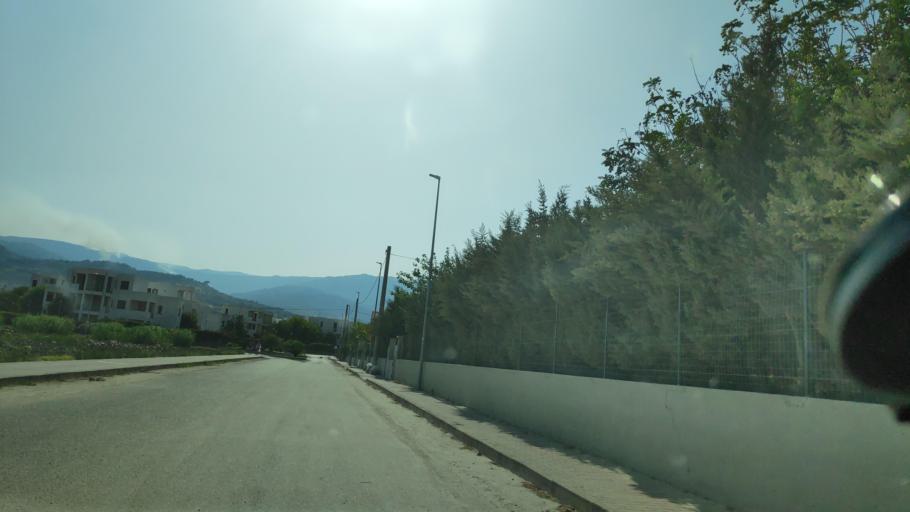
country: IT
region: Calabria
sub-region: Provincia di Catanzaro
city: Isca Marina
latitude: 38.6021
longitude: 16.5654
